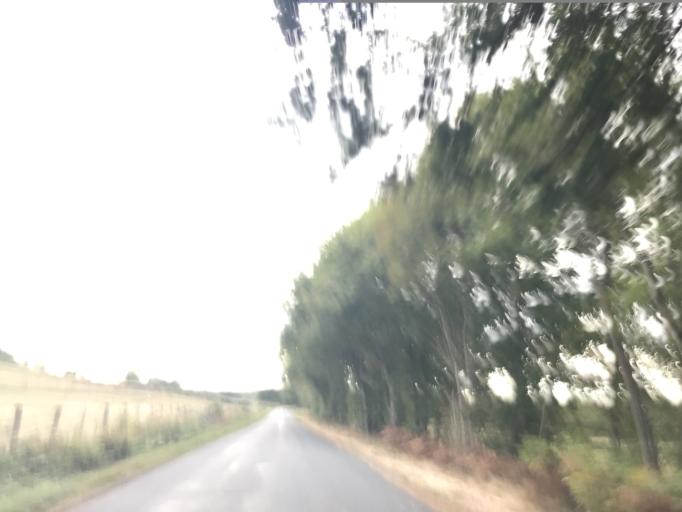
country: FR
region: Auvergne
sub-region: Departement du Puy-de-Dome
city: Courpiere
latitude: 45.7832
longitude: 3.5606
